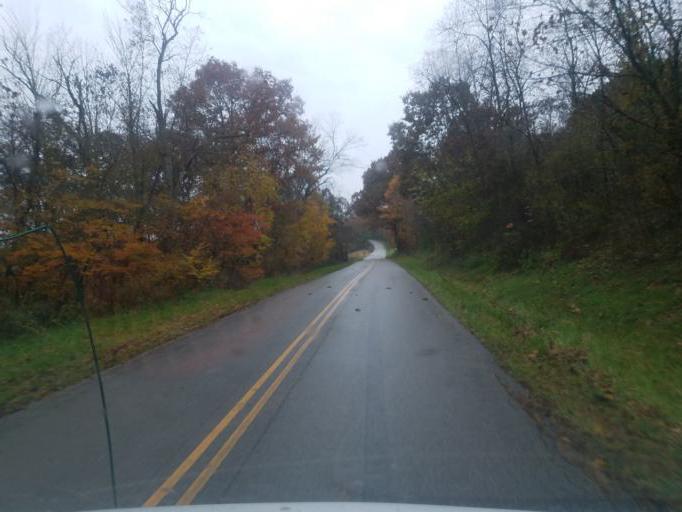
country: US
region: West Virginia
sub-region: Wood County
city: Vienna
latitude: 39.4239
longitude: -81.6134
